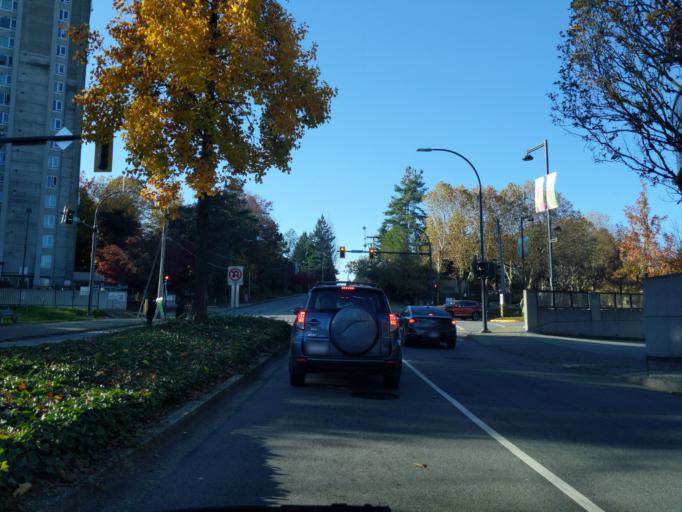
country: CA
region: British Columbia
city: New Westminster
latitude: 49.1859
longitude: -122.8513
